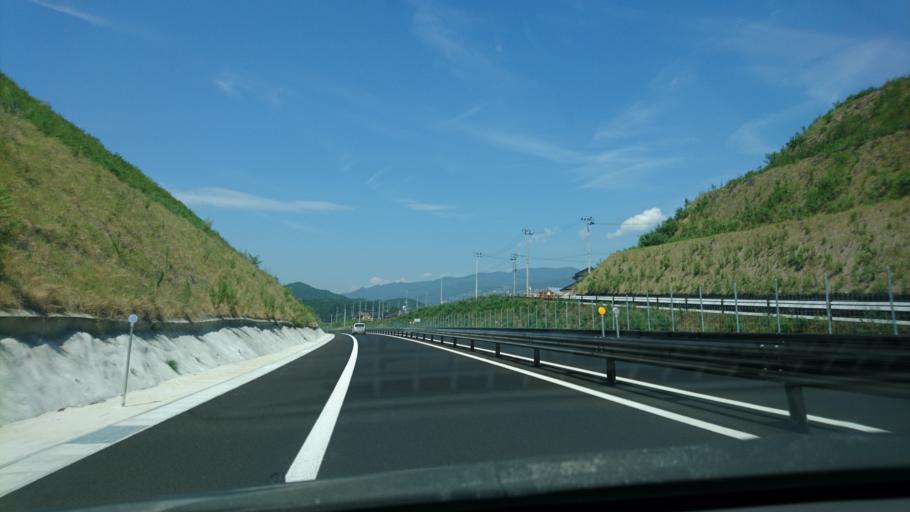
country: JP
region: Iwate
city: Ofunato
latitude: 38.9996
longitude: 141.6149
